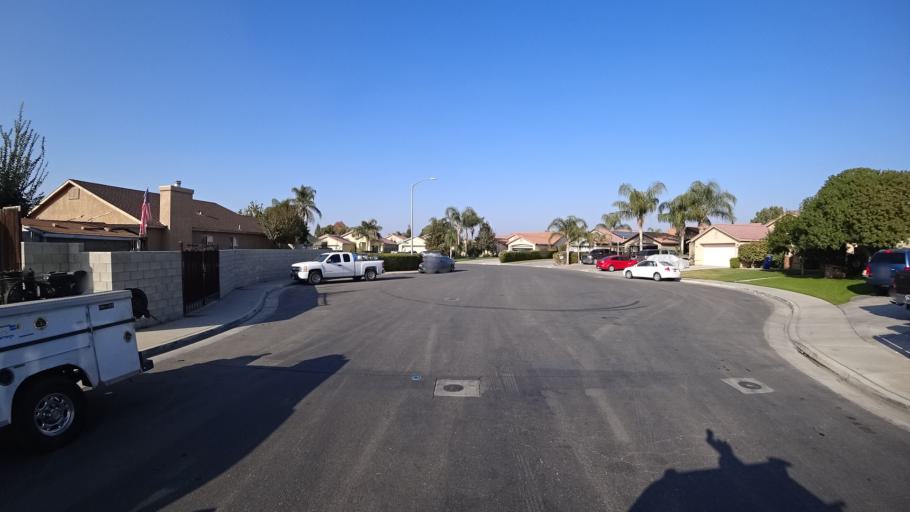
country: US
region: California
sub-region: Kern County
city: Greenfield
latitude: 35.2849
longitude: -119.0147
